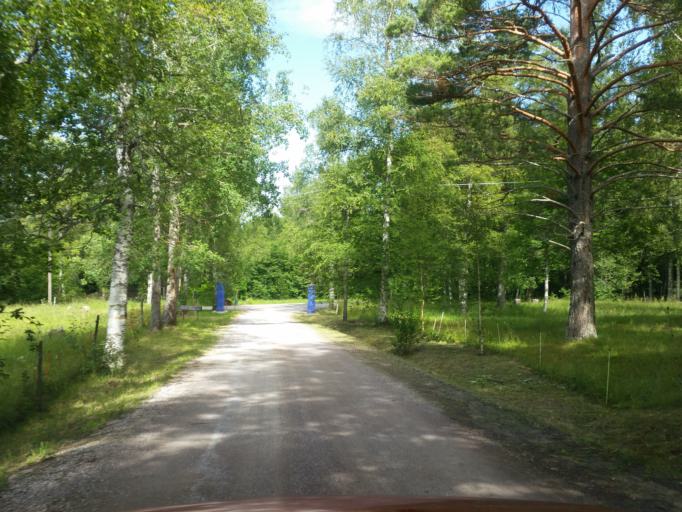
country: SE
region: Dalarna
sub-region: Gagnefs Kommun
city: Gagnef
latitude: 60.6598
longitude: 15.1215
